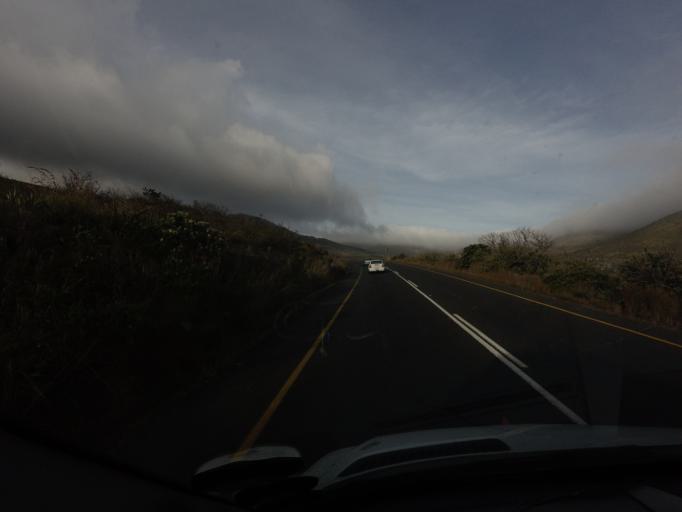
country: ZA
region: Western Cape
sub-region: City of Cape Town
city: Bergvliet
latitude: -34.1073
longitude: 18.4038
